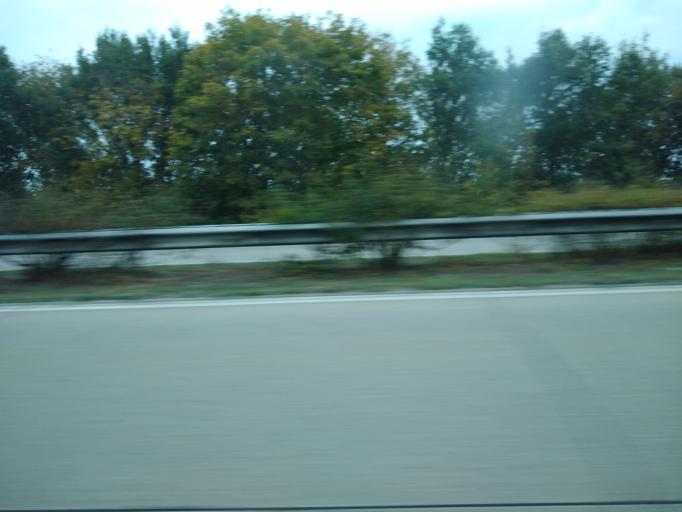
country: DE
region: Lower Saxony
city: Oldenburg
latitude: 53.1250
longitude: 8.2753
